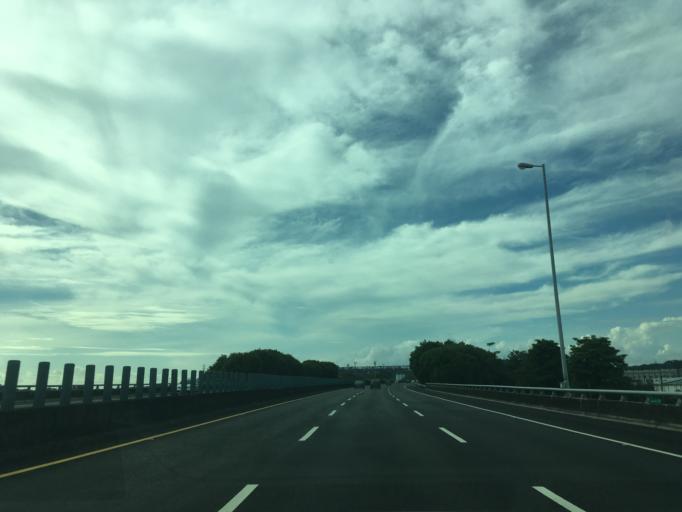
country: TW
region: Taiwan
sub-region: Chiayi
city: Jiayi Shi
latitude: 23.5091
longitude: 120.4877
